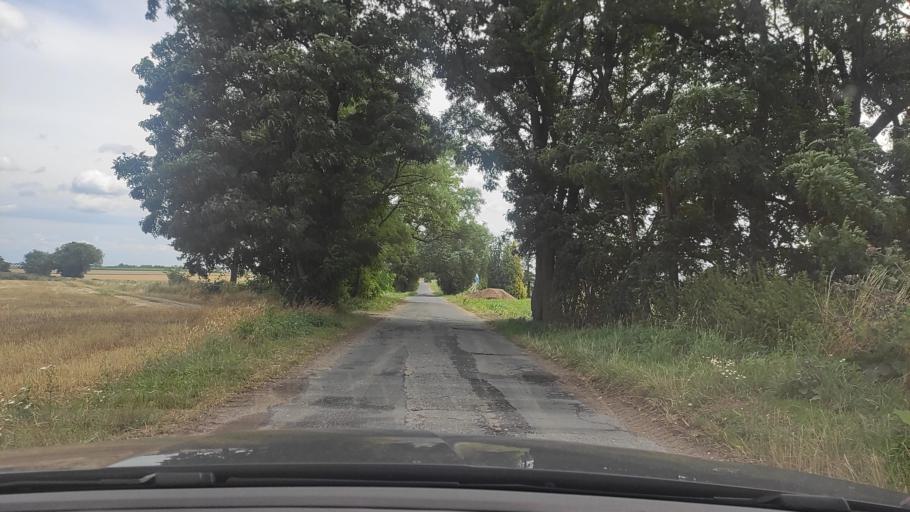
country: PL
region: Greater Poland Voivodeship
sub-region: Powiat poznanski
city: Kostrzyn
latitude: 52.4073
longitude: 17.1950
